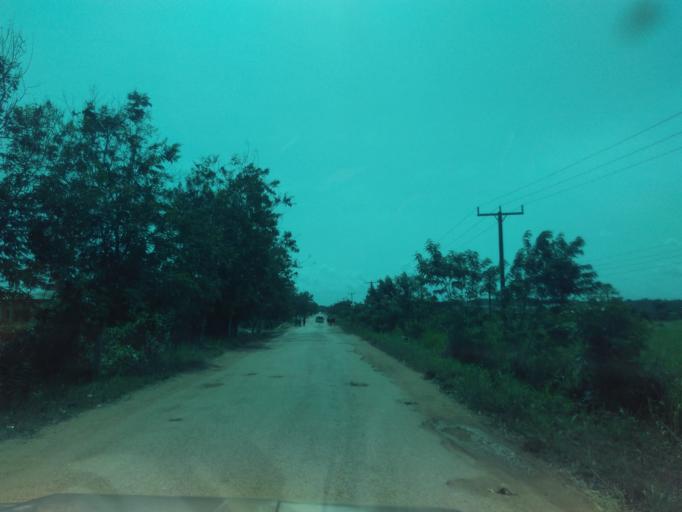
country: GH
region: Central
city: Elmina
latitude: 5.0923
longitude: -1.3764
